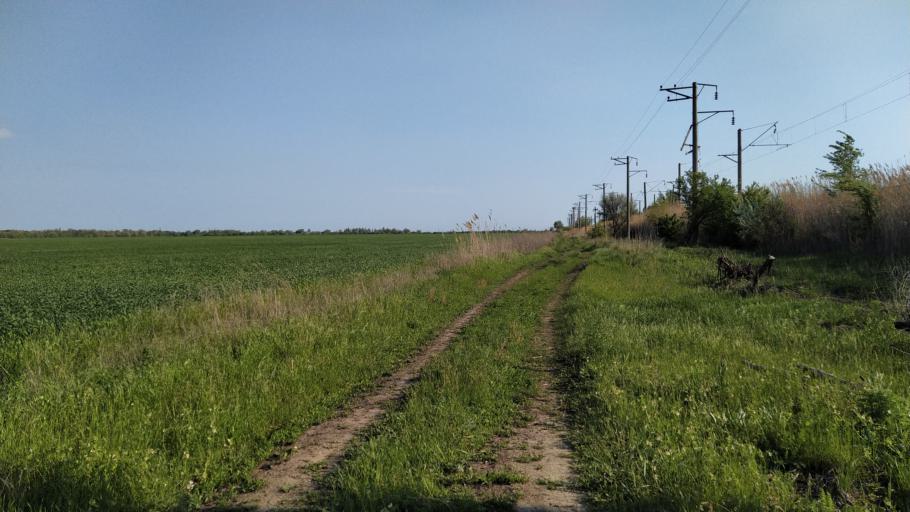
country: RU
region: Rostov
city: Bataysk
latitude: 47.1176
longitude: 39.7138
